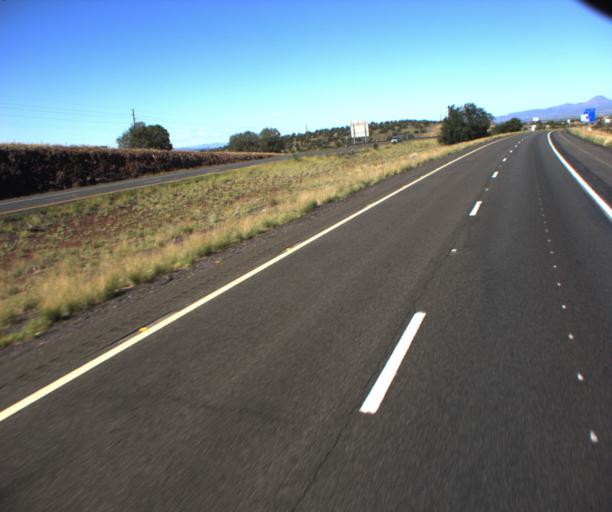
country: US
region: Arizona
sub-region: Coconino County
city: Williams
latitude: 35.2192
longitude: -112.4846
